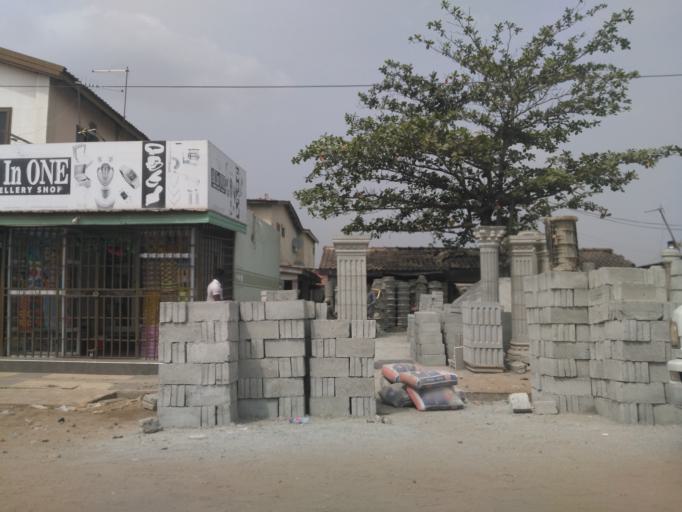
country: GH
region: Greater Accra
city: Nungua
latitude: 5.6014
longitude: -0.0798
